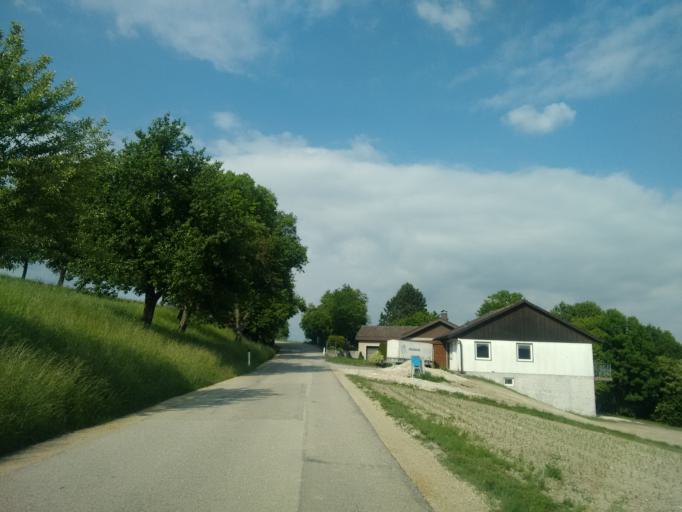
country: AT
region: Upper Austria
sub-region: Politischer Bezirk Grieskirchen
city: Bad Schallerbach
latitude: 48.1898
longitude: 13.8994
